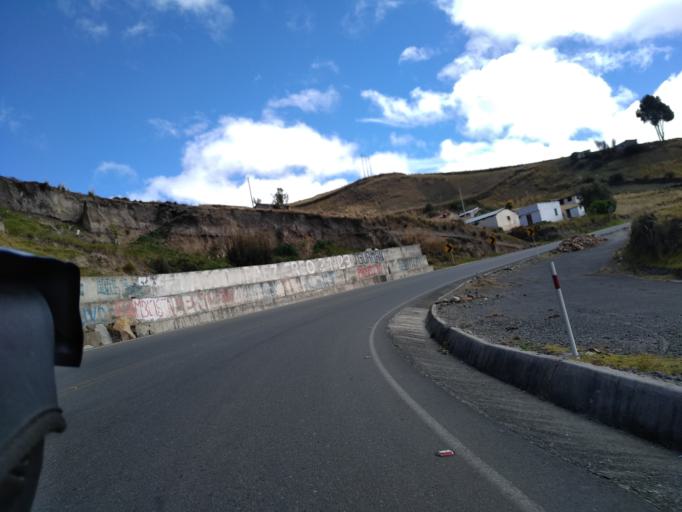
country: EC
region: Cotopaxi
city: Pujili
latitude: -0.9652
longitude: -78.9064
